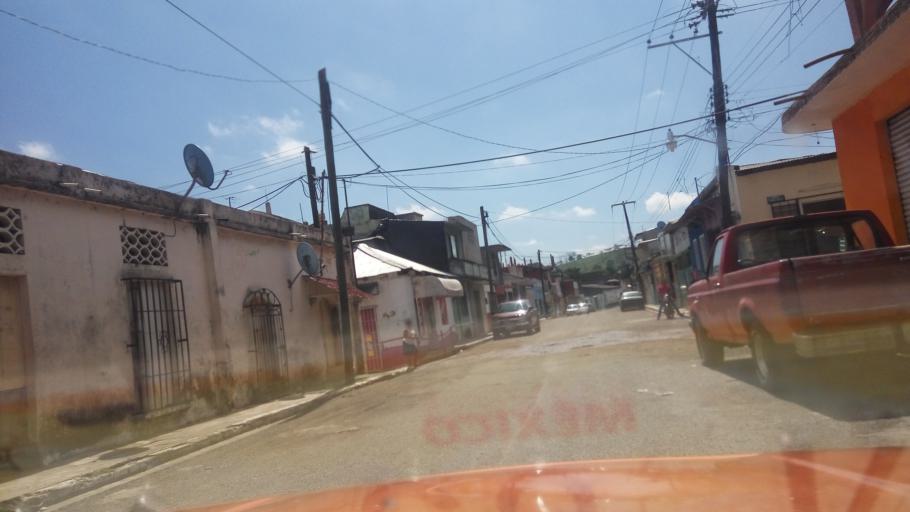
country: MX
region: Tabasco
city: Teapa
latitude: 17.5472
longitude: -92.9523
